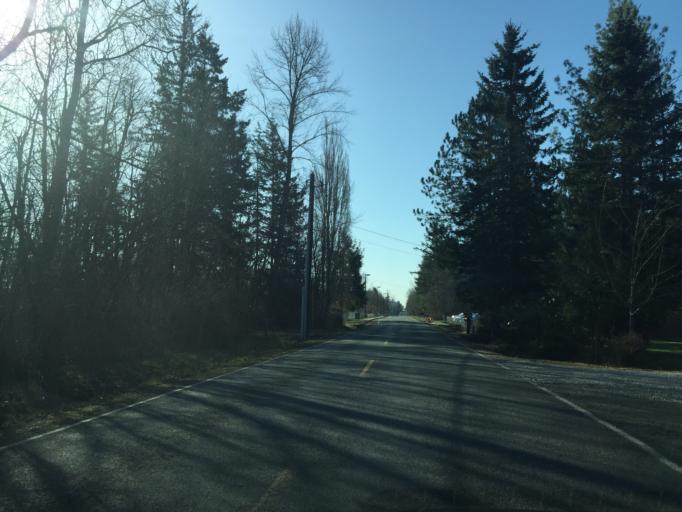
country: US
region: Washington
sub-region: Whatcom County
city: Marietta-Alderwood
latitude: 48.8034
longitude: -122.5081
